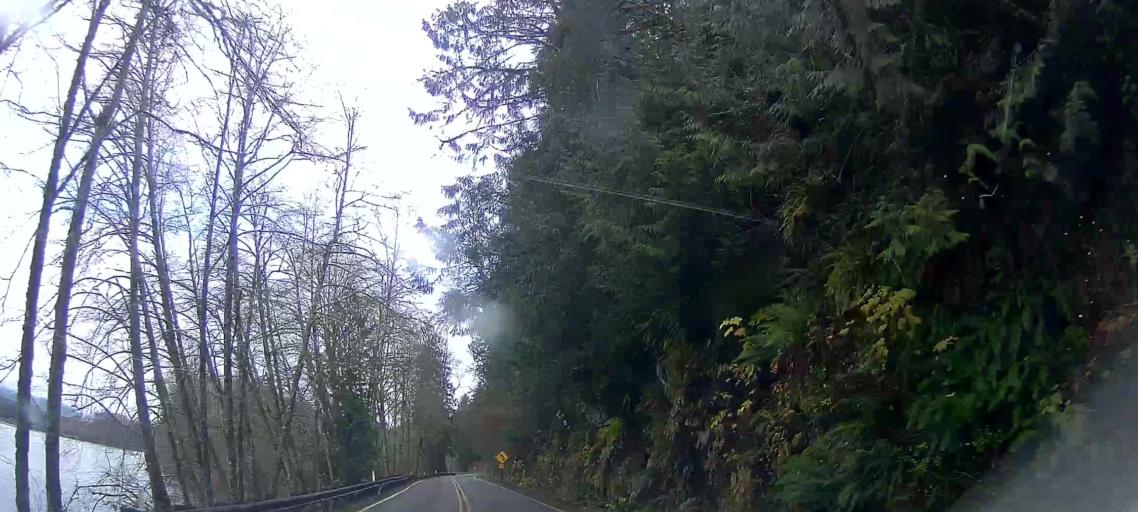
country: US
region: Washington
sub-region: Skagit County
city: Sedro-Woolley
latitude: 48.5152
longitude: -121.9762
